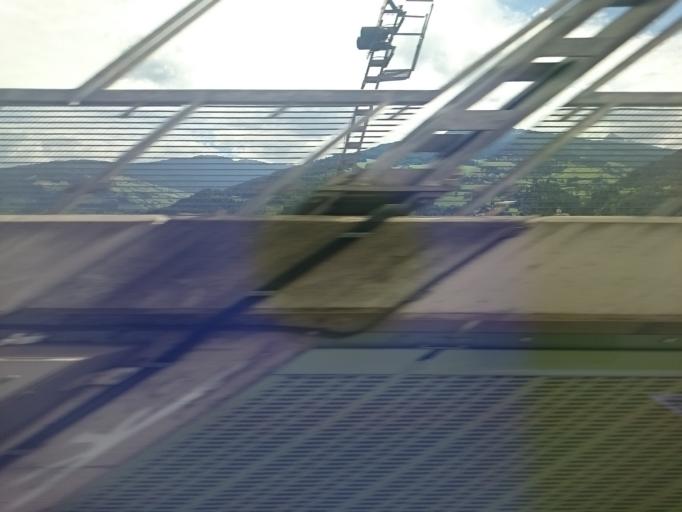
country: AT
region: Tyrol
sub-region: Politischer Bezirk Innsbruck Land
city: Baumkirchen
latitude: 47.2920
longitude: 11.5572
